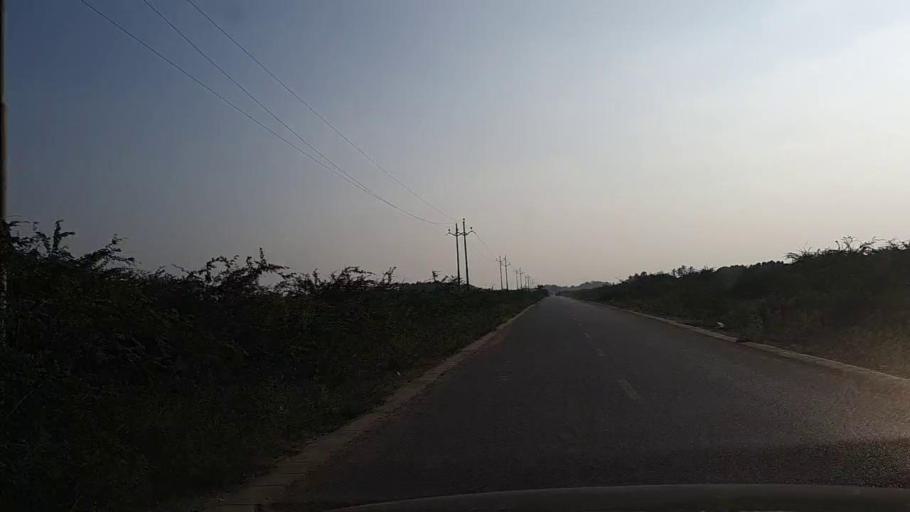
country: PK
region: Sindh
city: Gharo
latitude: 24.7892
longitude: 67.5152
